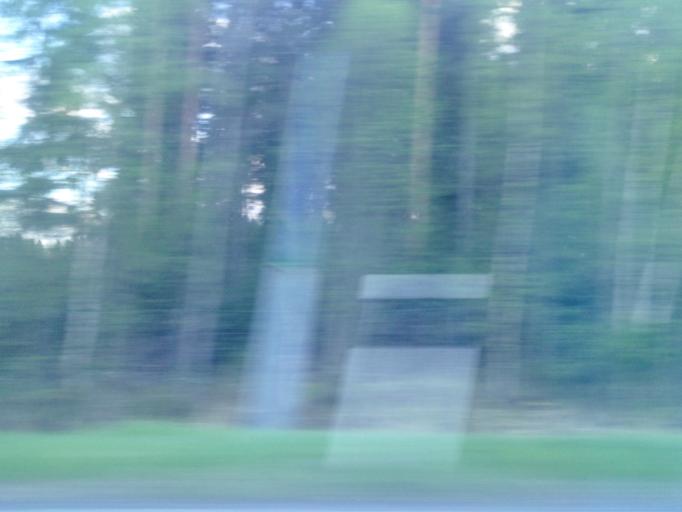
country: FI
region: Haeme
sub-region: Haemeenlinna
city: Kalvola
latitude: 61.1032
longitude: 24.1538
